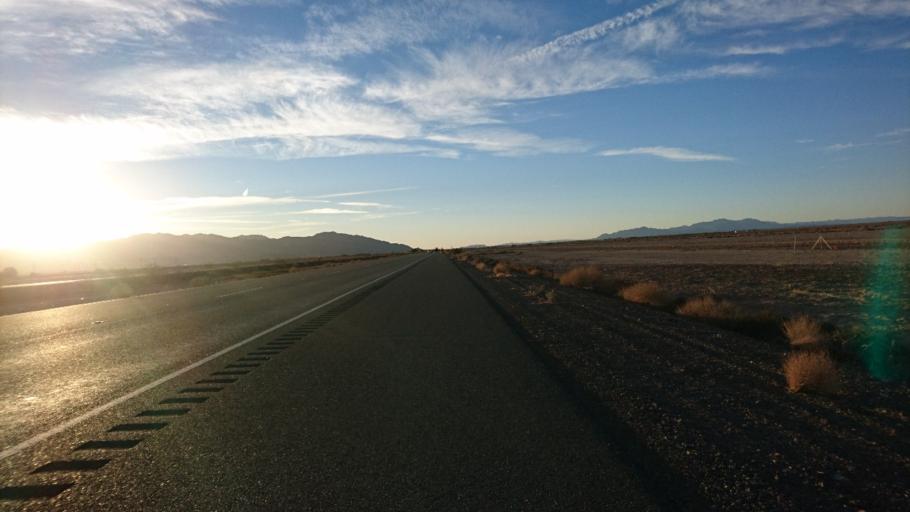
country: US
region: California
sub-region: San Bernardino County
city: Fort Irwin
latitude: 34.8057
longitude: -116.5495
